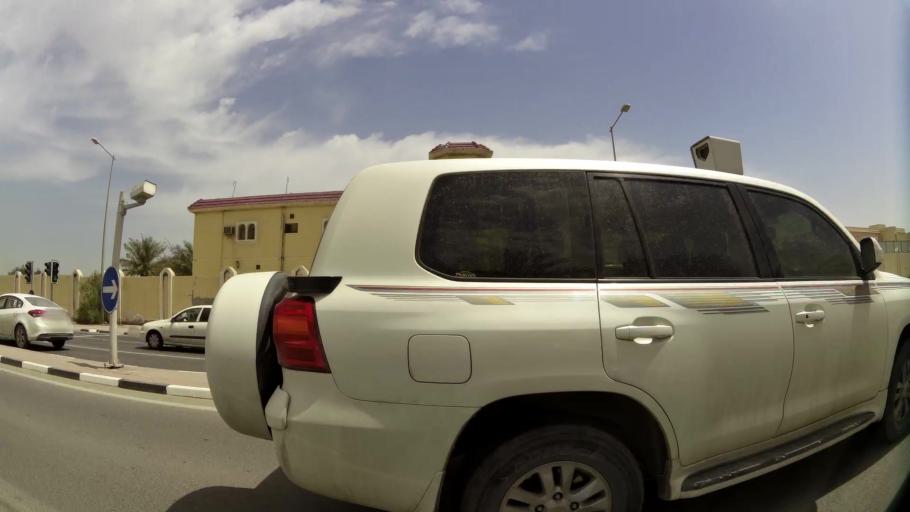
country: QA
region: Baladiyat ar Rayyan
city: Ar Rayyan
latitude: 25.2792
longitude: 51.4202
